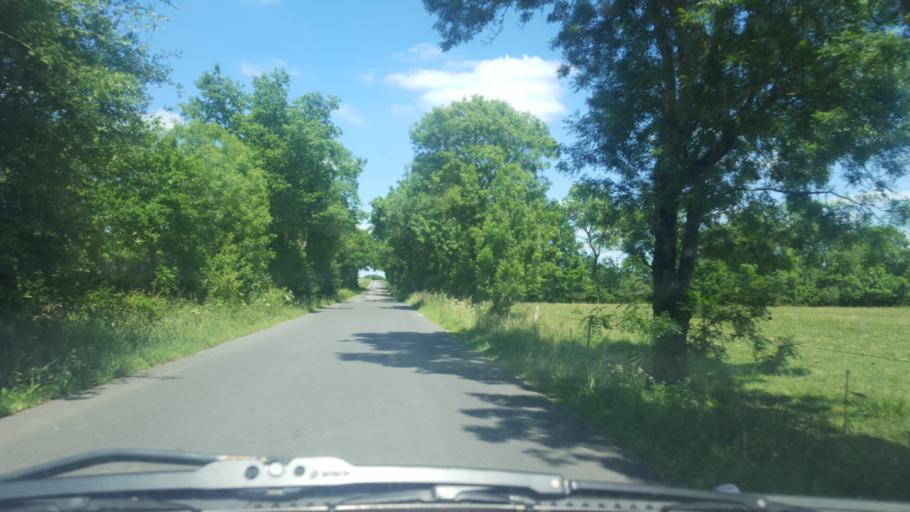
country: FR
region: Pays de la Loire
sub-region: Departement de la Loire-Atlantique
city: La Limouziniere
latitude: 47.0171
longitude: -1.6076
